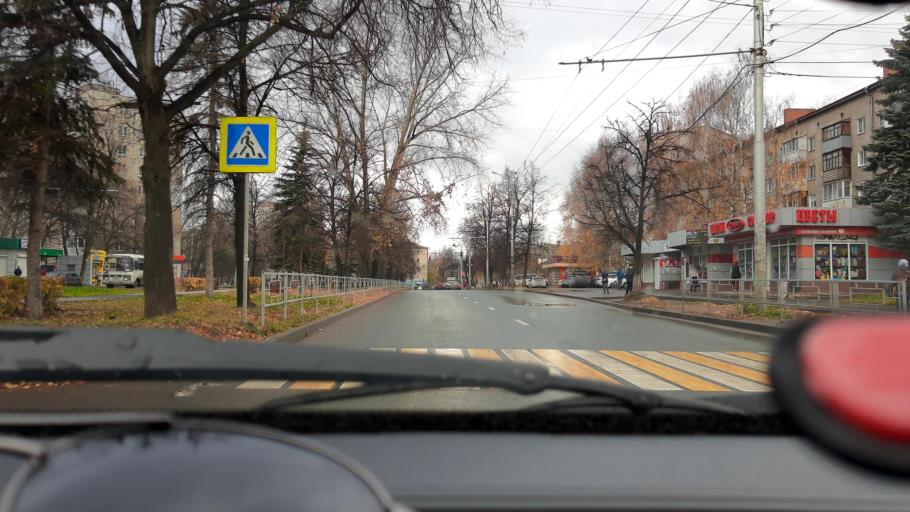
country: RU
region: Bashkortostan
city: Ufa
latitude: 54.8115
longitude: 56.1204
